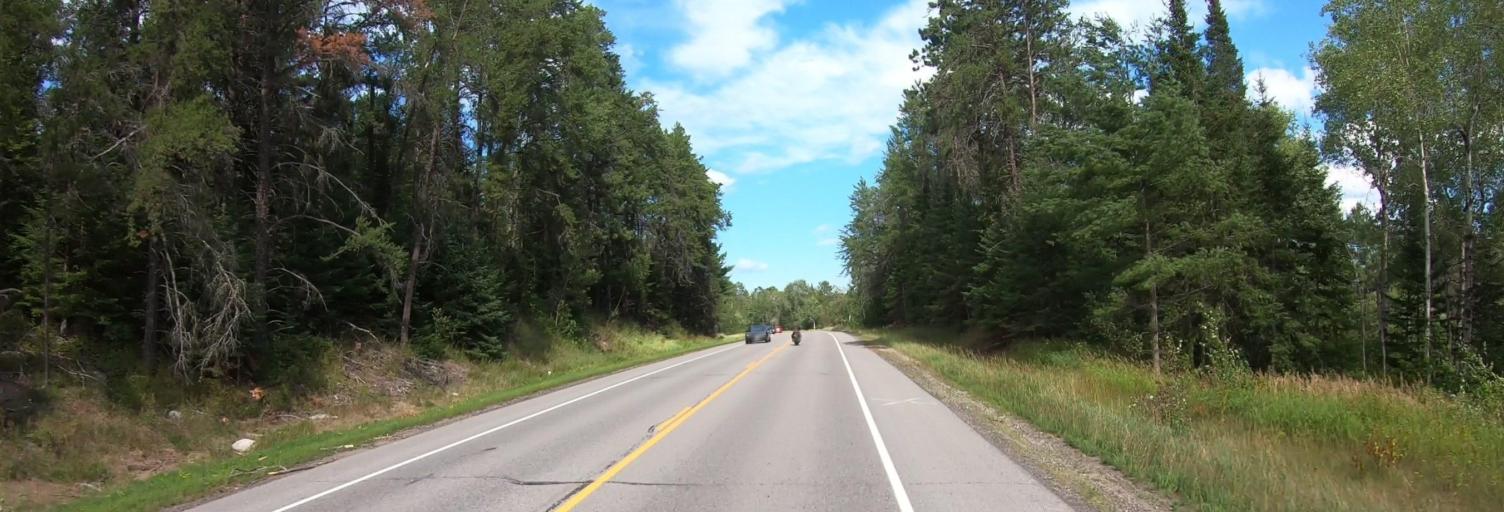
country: US
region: Minnesota
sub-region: Saint Louis County
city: Aurora
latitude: 47.8073
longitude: -92.2609
